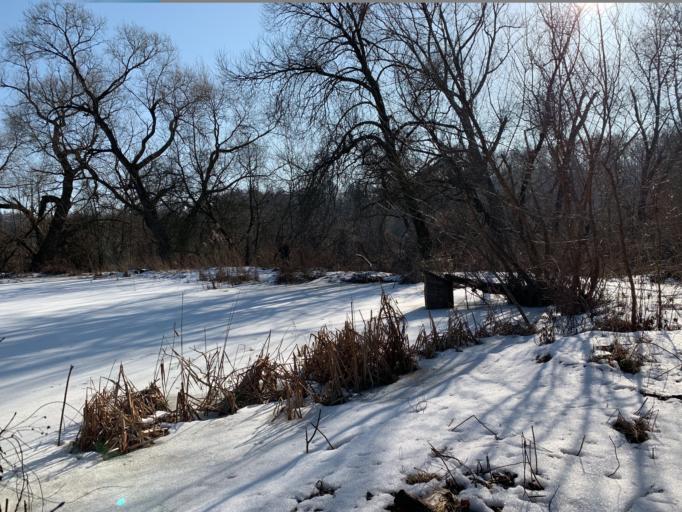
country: BY
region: Minsk
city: Nyasvizh
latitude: 53.2005
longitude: 26.6420
